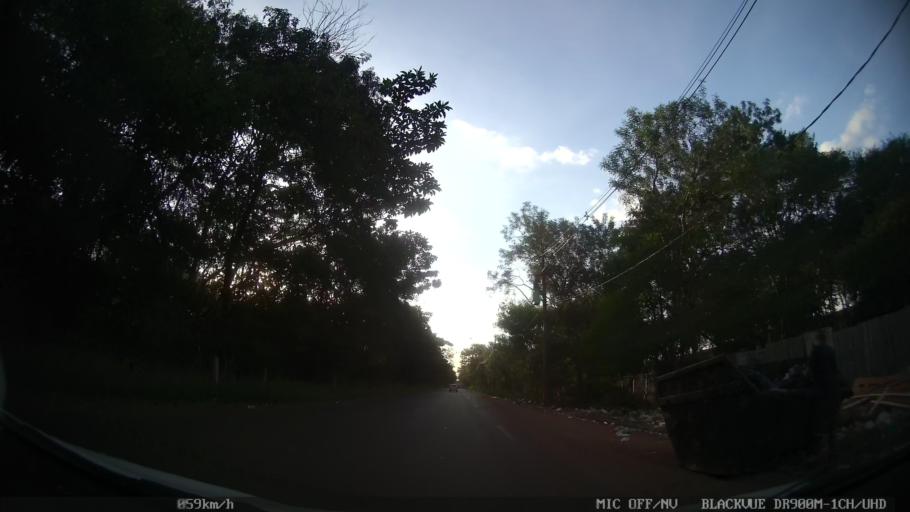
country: BR
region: Sao Paulo
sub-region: Ribeirao Preto
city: Ribeirao Preto
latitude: -21.1124
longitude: -47.8067
